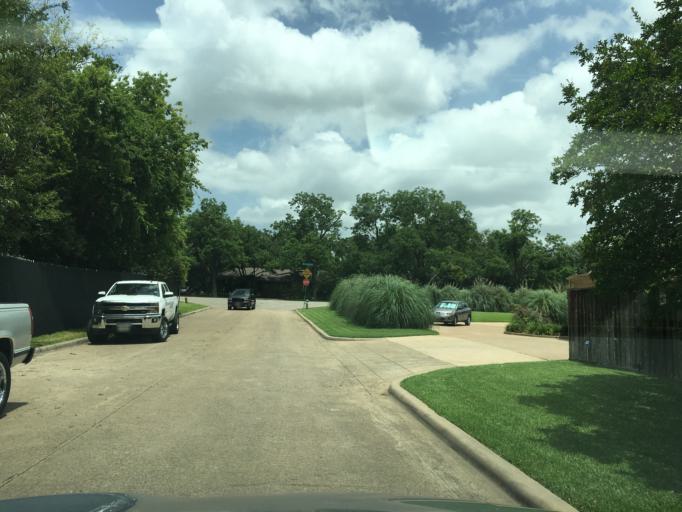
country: US
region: Texas
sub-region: Dallas County
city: University Park
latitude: 32.9013
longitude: -96.7931
